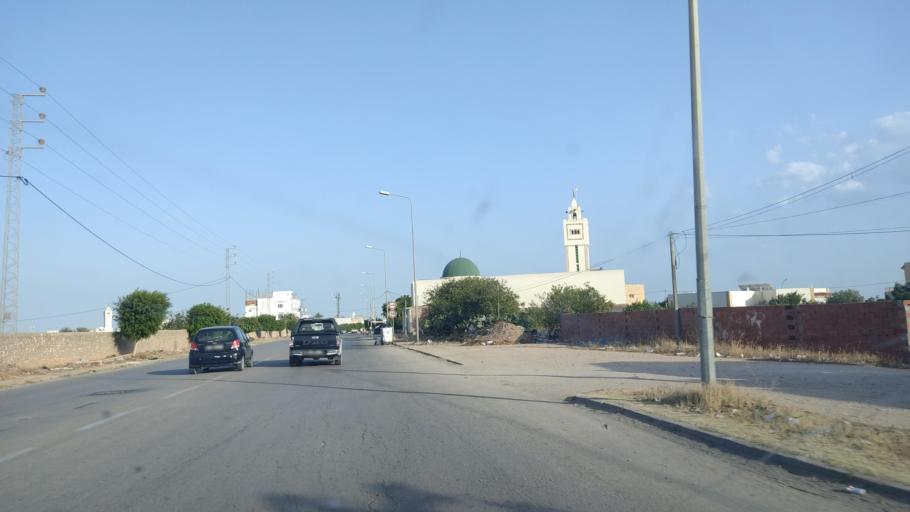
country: TN
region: Safaqis
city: Sfax
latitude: 34.7919
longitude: 10.6861
